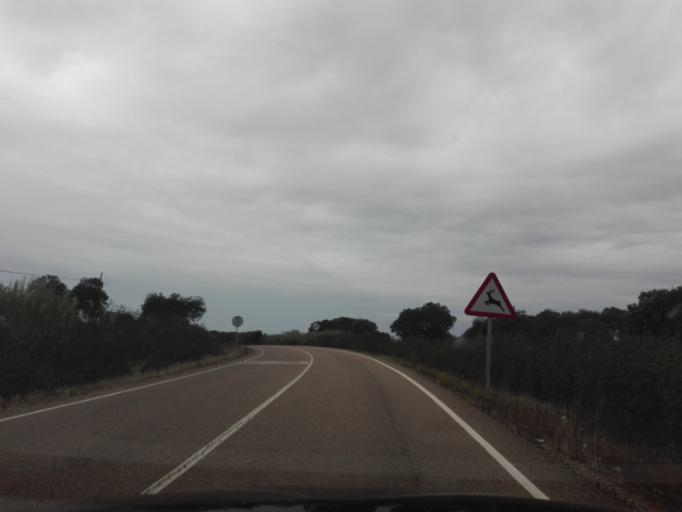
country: ES
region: Extremadura
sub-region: Provincia de Badajoz
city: Alburquerque
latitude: 39.2004
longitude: -6.9988
